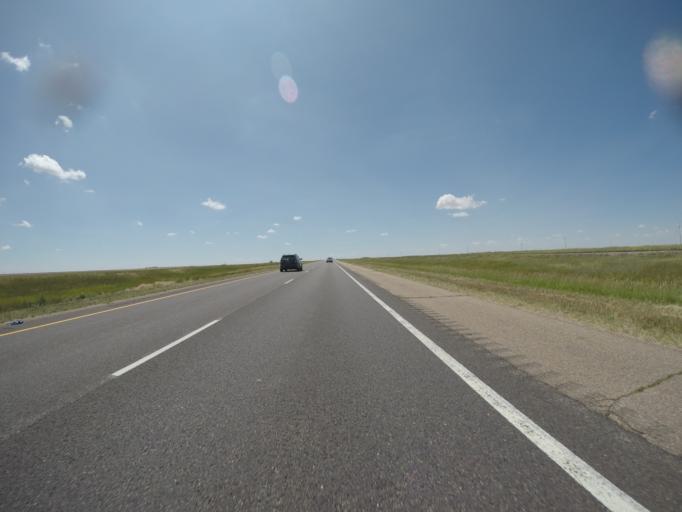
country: US
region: Colorado
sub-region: Lincoln County
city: Hugo
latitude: 39.2824
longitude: -103.3098
